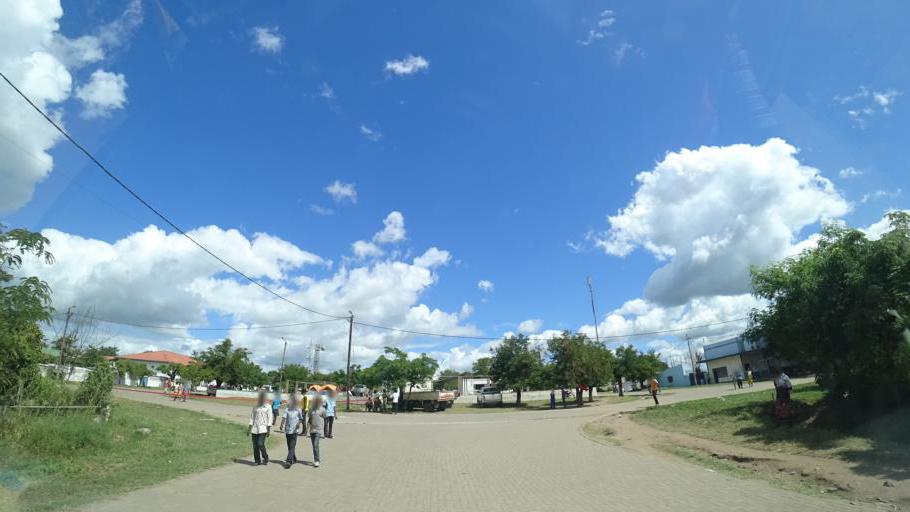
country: MZ
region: Sofala
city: Dondo
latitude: -19.2720
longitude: 34.2062
